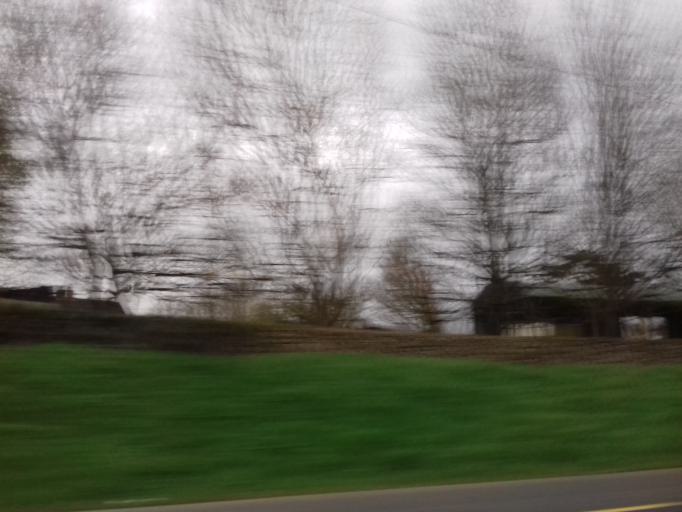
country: IE
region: Munster
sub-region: County Limerick
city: Rathkeale
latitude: 52.5043
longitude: -8.9913
